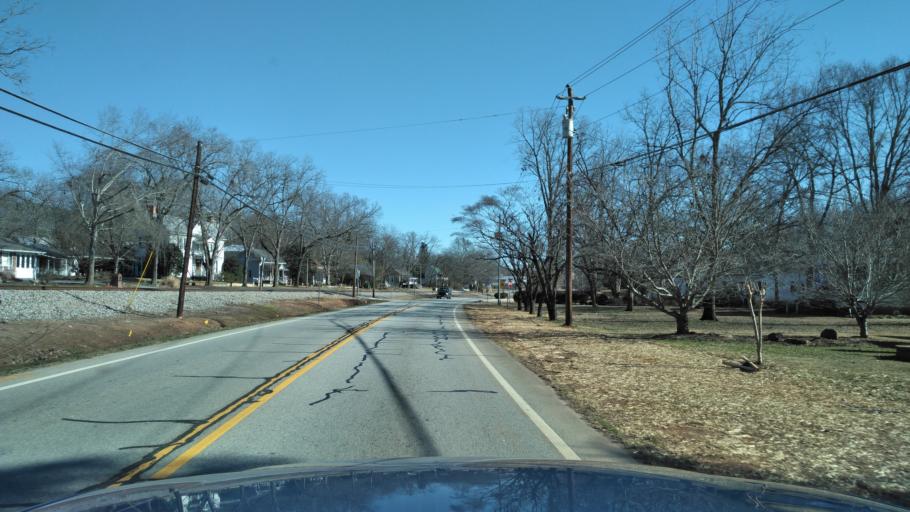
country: US
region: Georgia
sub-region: Banks County
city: Maysville
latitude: 34.2562
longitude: -83.5652
